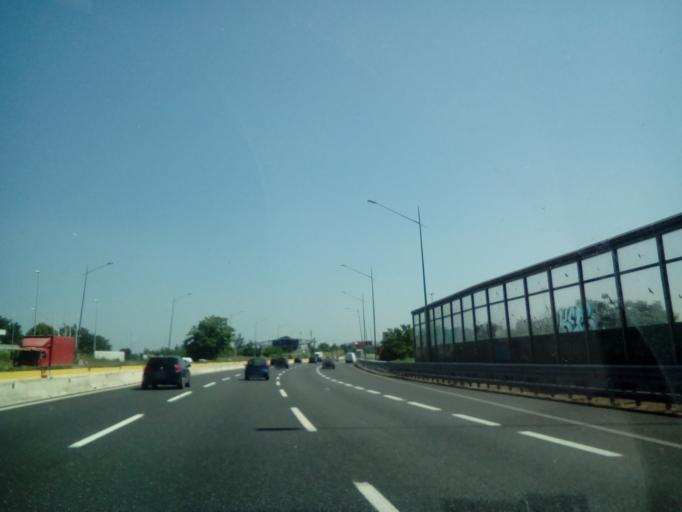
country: IT
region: Latium
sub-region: Citta metropolitana di Roma Capitale
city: Valle Santa
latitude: 41.9569
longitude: 12.3853
